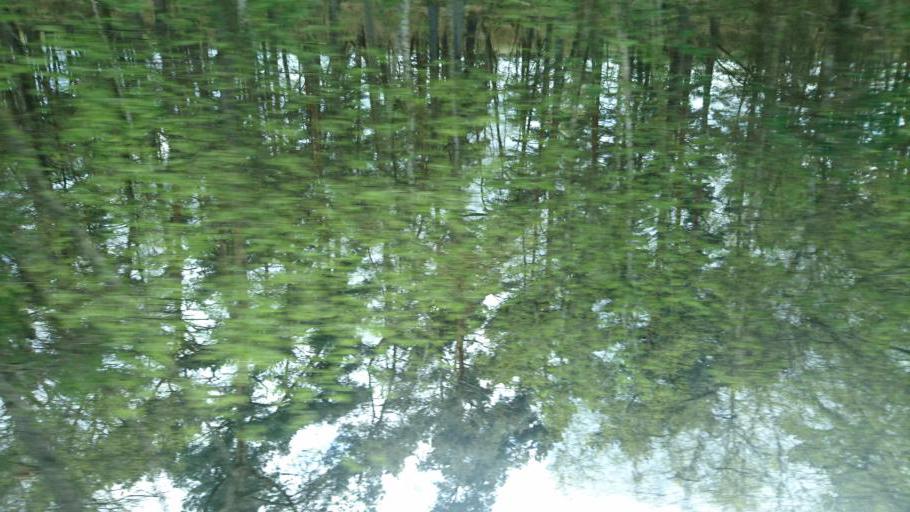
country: DE
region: Mecklenburg-Vorpommern
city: Zingst
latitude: 54.4230
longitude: 12.6511
